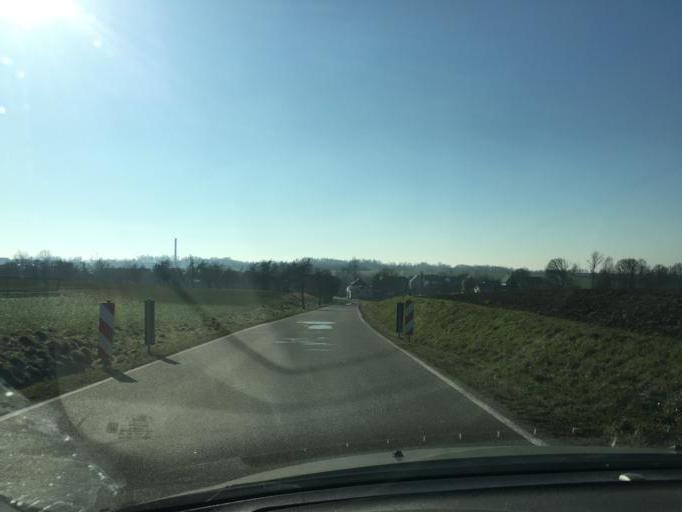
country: DE
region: Saxony
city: Narsdorf
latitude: 51.0217
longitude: 12.7103
